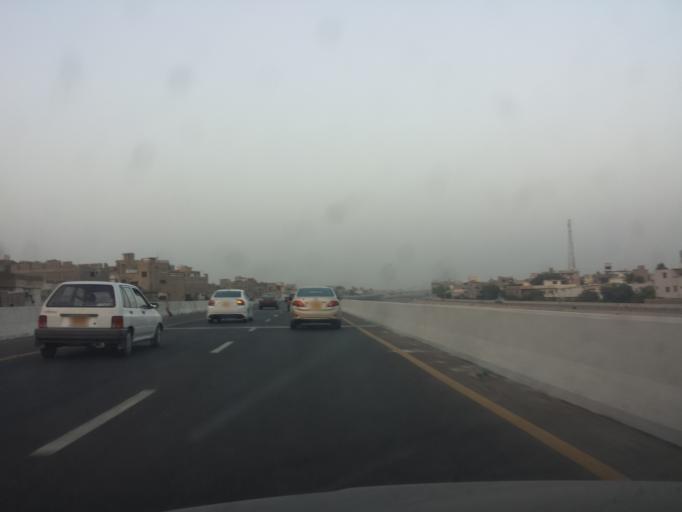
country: PK
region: Sindh
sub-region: Karachi District
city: Karachi
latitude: 24.8953
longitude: 67.0482
